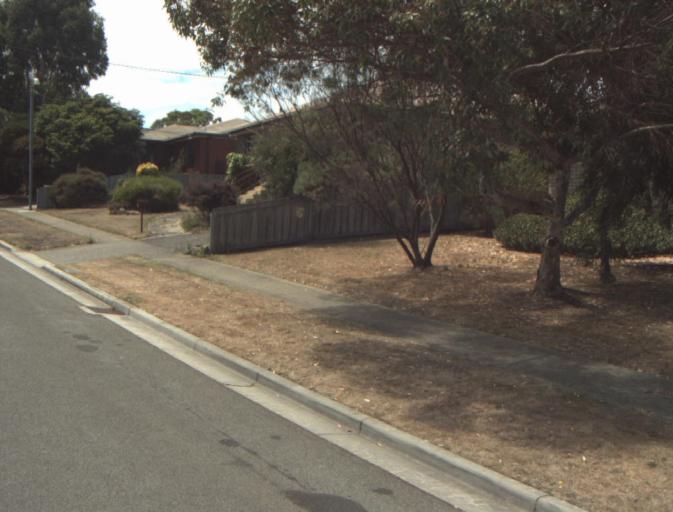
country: AU
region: Tasmania
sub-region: Launceston
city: Mayfield
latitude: -41.3791
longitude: 147.1161
